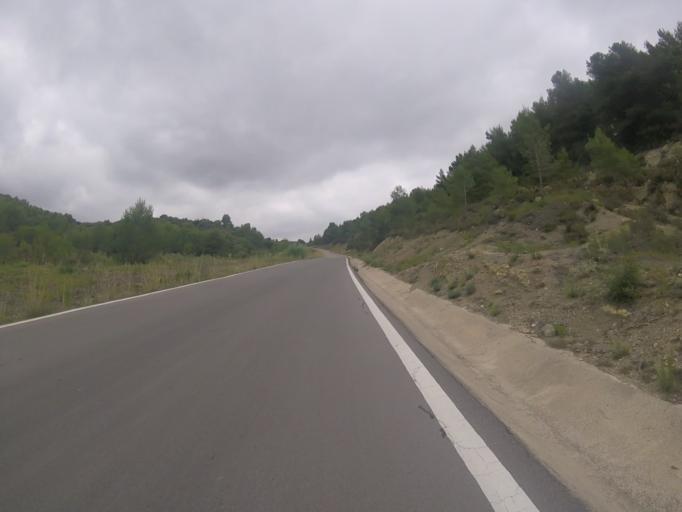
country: ES
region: Valencia
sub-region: Provincia de Castello
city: Cabanes
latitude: 40.1191
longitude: 0.0472
